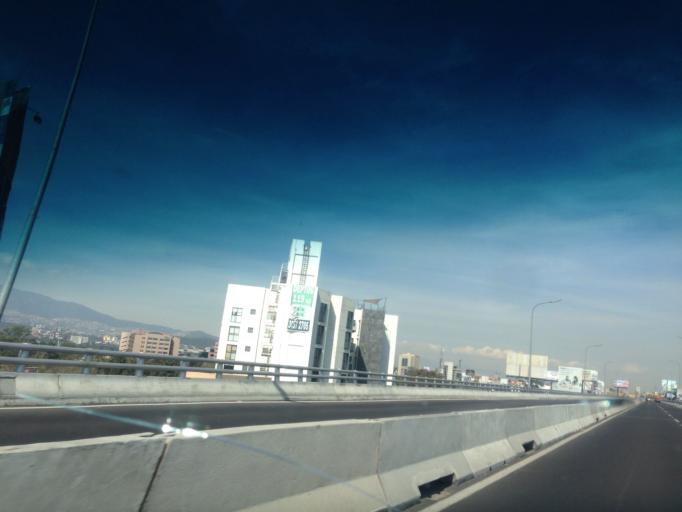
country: MX
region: Mexico City
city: Tlalpan
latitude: 19.2957
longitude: -99.1558
